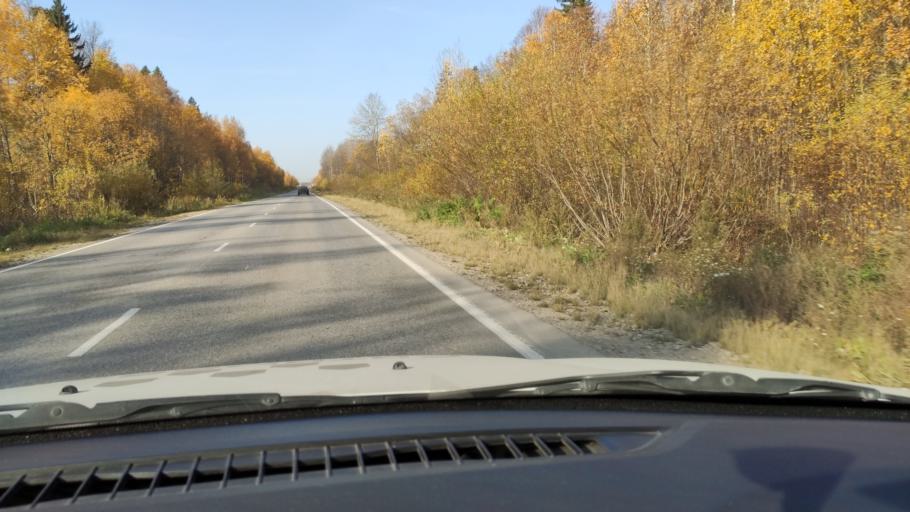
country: RU
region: Perm
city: Novyye Lyady
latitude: 58.0264
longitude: 56.6315
